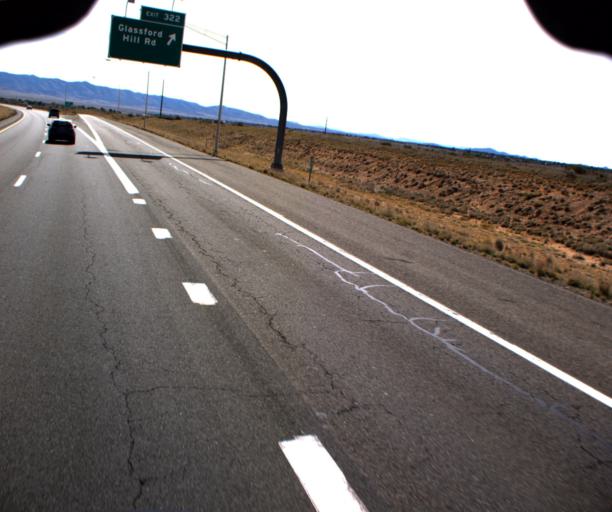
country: US
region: Arizona
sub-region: Yavapai County
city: Prescott Valley
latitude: 34.6303
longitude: -112.3634
